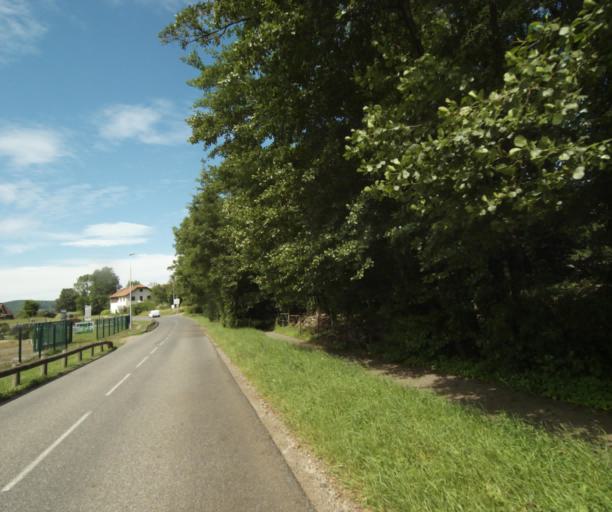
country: FR
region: Rhone-Alpes
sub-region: Departement de la Haute-Savoie
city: Perrignier
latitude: 46.2876
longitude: 6.4467
